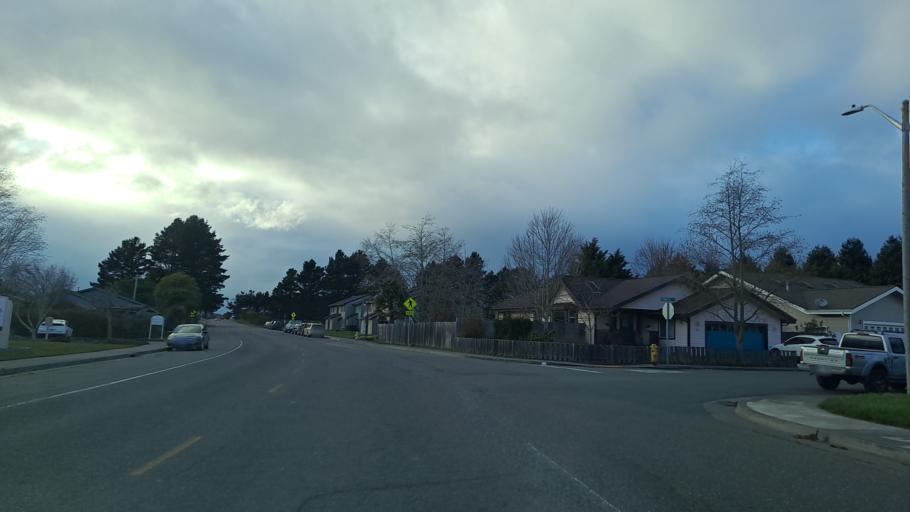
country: US
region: California
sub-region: Humboldt County
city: Fortuna
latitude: 40.5846
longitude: -124.1395
